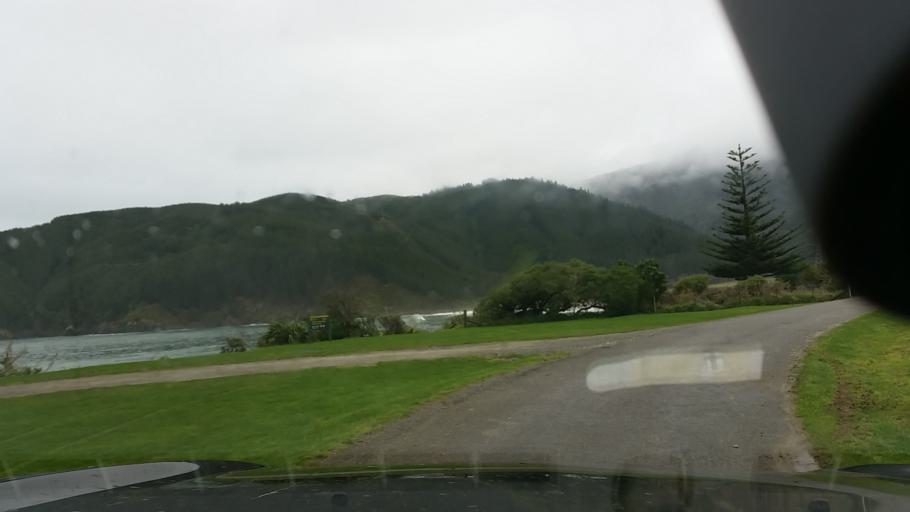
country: NZ
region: Marlborough
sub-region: Marlborough District
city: Picton
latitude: -41.3544
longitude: 174.0770
